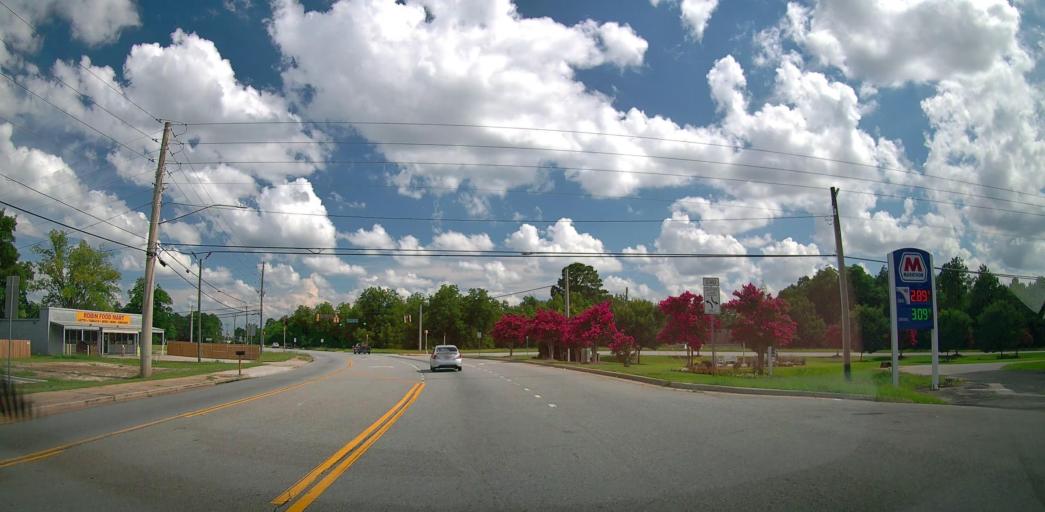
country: US
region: Georgia
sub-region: Houston County
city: Centerville
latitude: 32.6024
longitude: -83.6613
